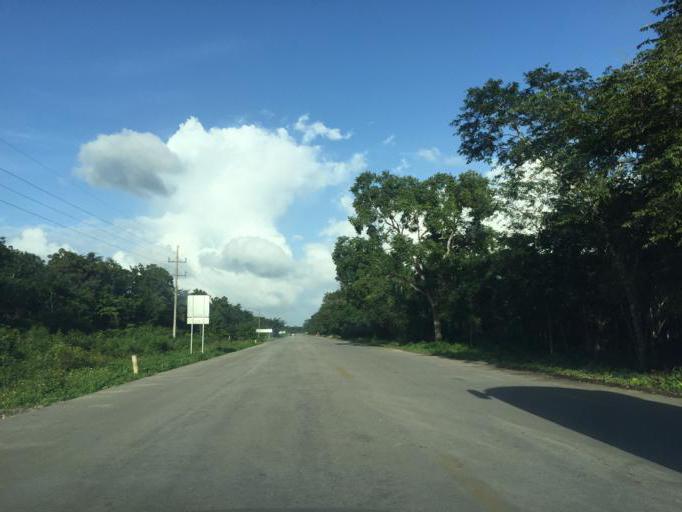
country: MX
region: Quintana Roo
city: Coba
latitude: 20.5009
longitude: -87.7301
